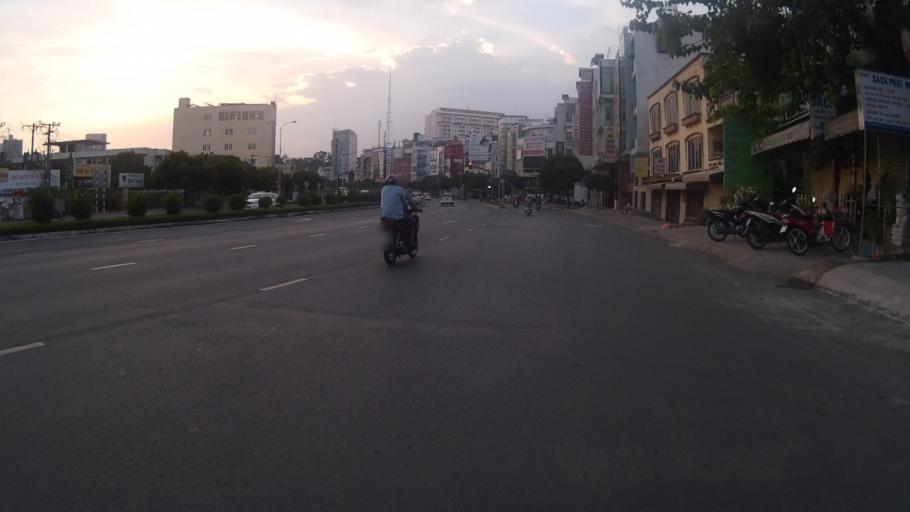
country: VN
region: Ho Chi Minh City
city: Quan Mot
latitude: 10.7898
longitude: 106.7117
